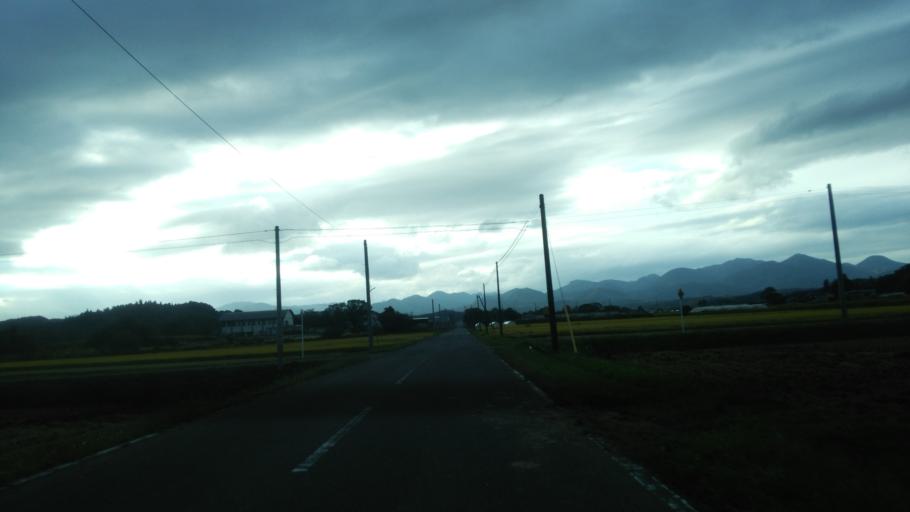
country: JP
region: Fukushima
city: Sukagawa
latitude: 37.2730
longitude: 140.2769
